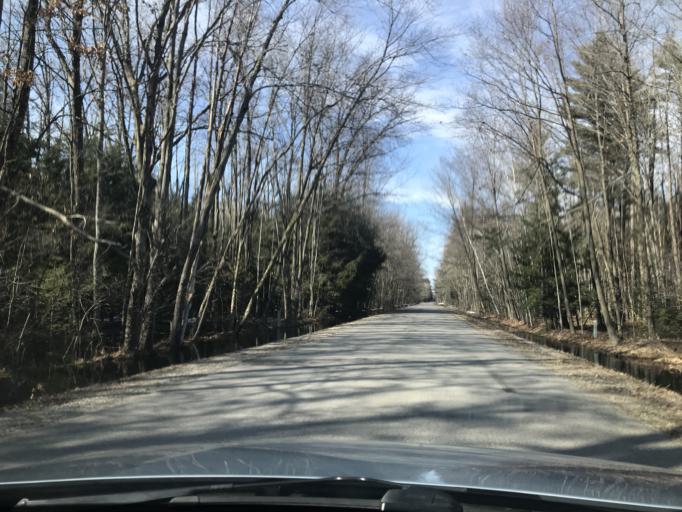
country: US
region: Wisconsin
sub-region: Marinette County
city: Marinette
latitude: 45.0231
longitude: -87.6673
